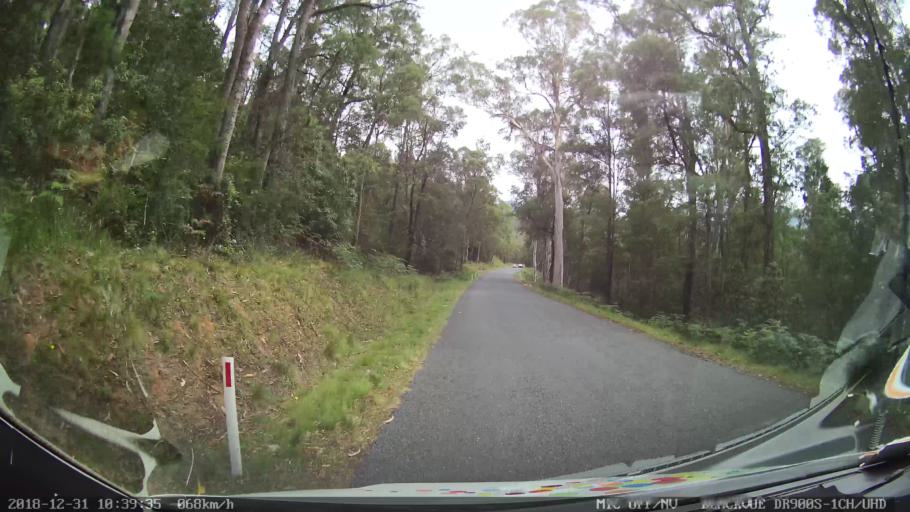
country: AU
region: New South Wales
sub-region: Snowy River
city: Jindabyne
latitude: -36.3976
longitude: 148.1769
